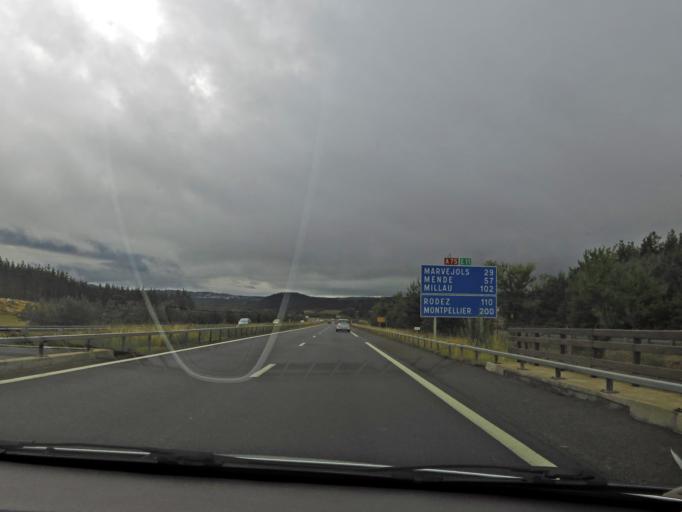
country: FR
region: Languedoc-Roussillon
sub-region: Departement de la Lozere
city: Aumont-Aubrac
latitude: 44.7706
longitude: 3.2842
